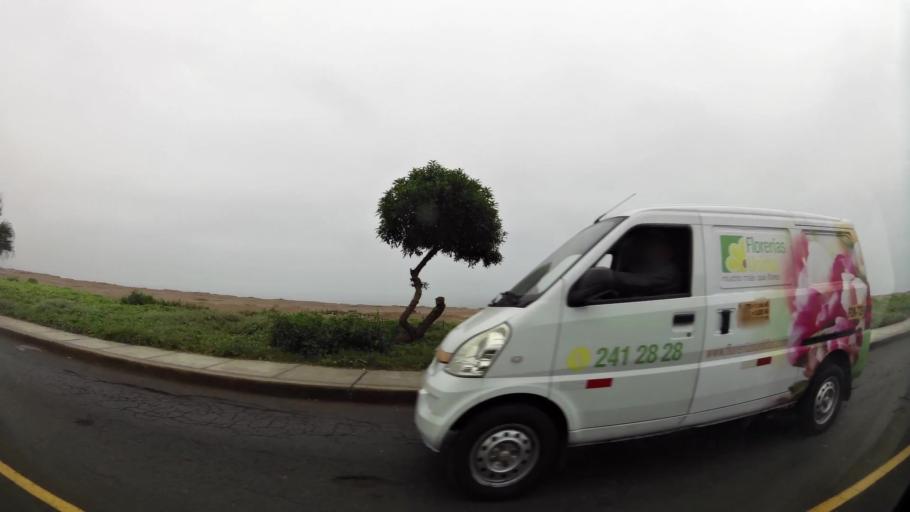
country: PE
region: Callao
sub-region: Callao
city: Callao
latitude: -12.0833
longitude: -77.1024
